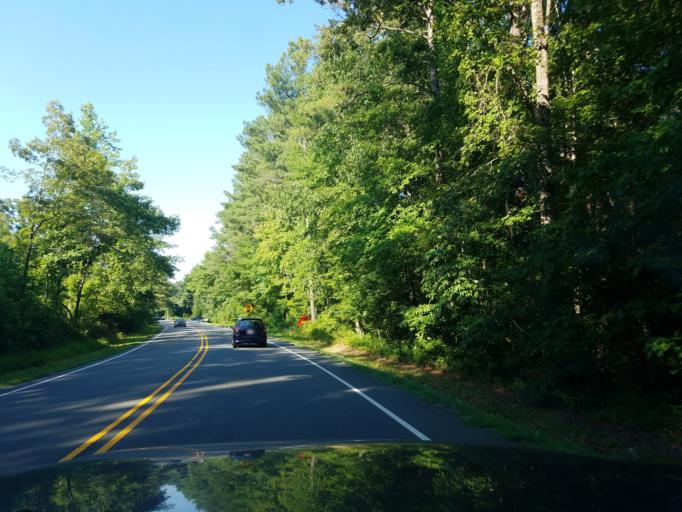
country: US
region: North Carolina
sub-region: Orange County
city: Chapel Hill
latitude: 35.8866
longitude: -78.9589
